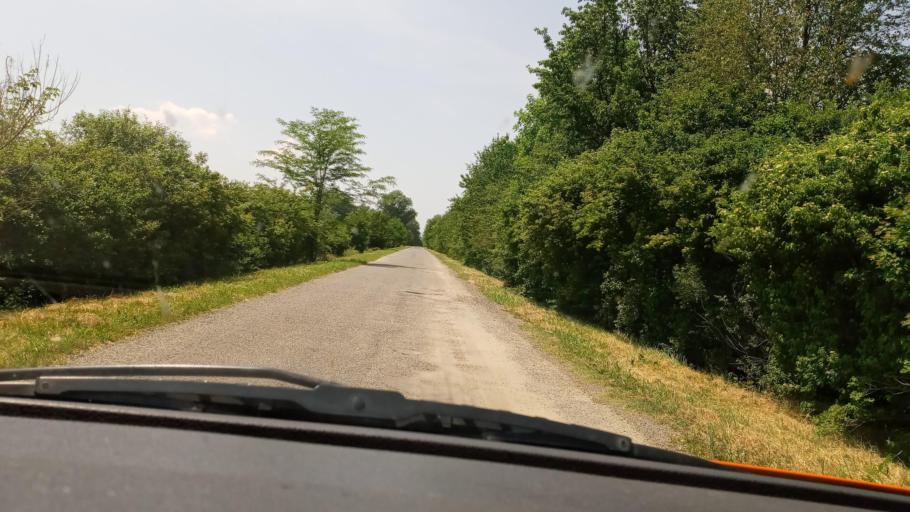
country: HU
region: Baranya
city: Sellye
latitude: 45.8095
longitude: 17.8616
